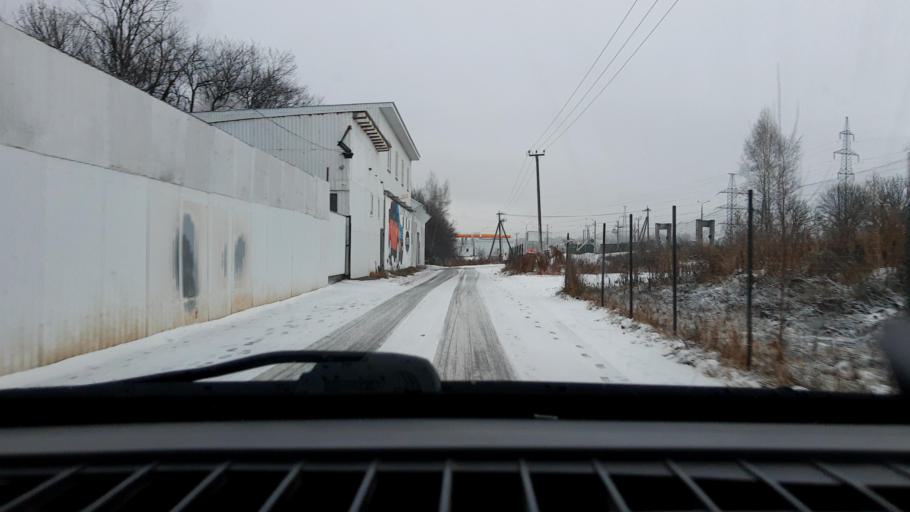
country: RU
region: Nizjnij Novgorod
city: Afonino
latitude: 56.2360
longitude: 44.0450
